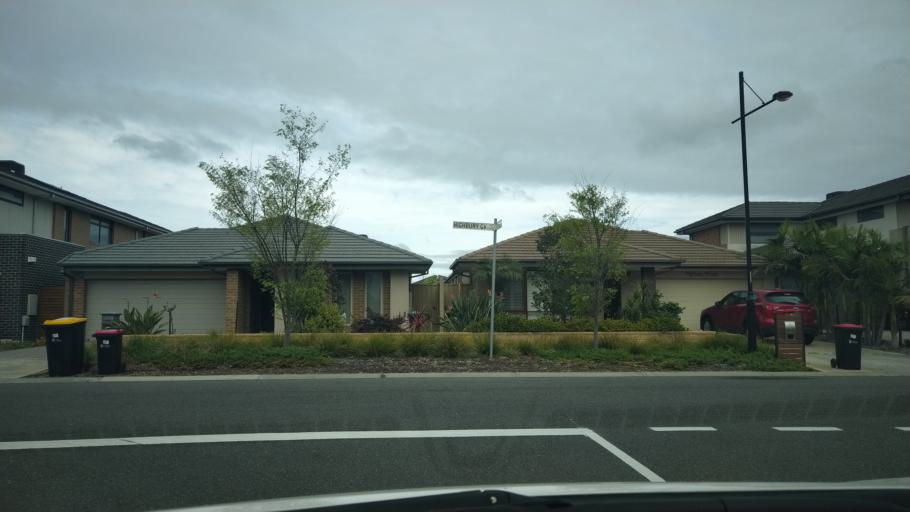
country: AU
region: Victoria
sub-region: Greater Dandenong
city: Keysborough
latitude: -38.0070
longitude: 145.1756
